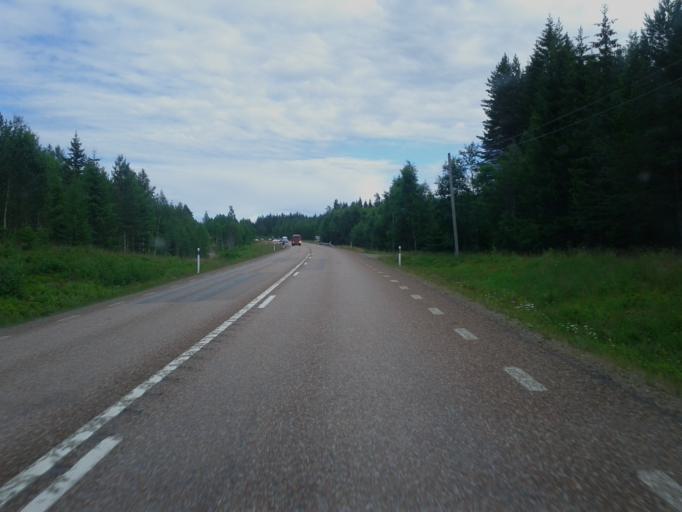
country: SE
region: Dalarna
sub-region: Faluns Kommun
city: Bjursas
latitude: 60.7873
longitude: 15.2857
